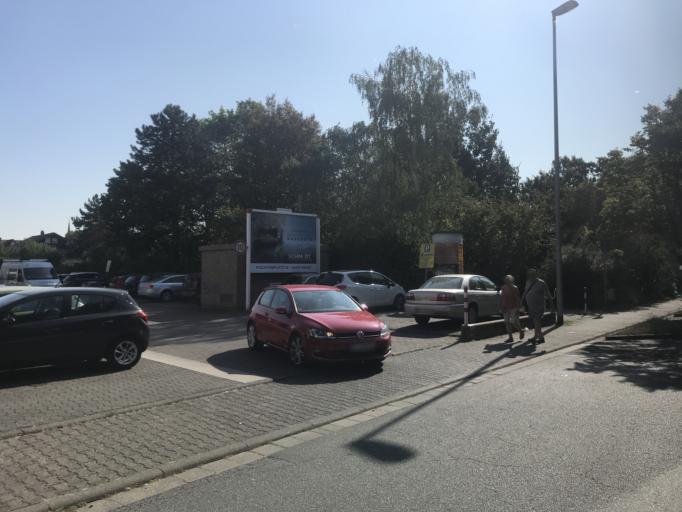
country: DE
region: Hesse
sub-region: Regierungsbezirk Darmstadt
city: Ginsheim-Gustavsburg
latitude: 49.9881
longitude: 8.3497
